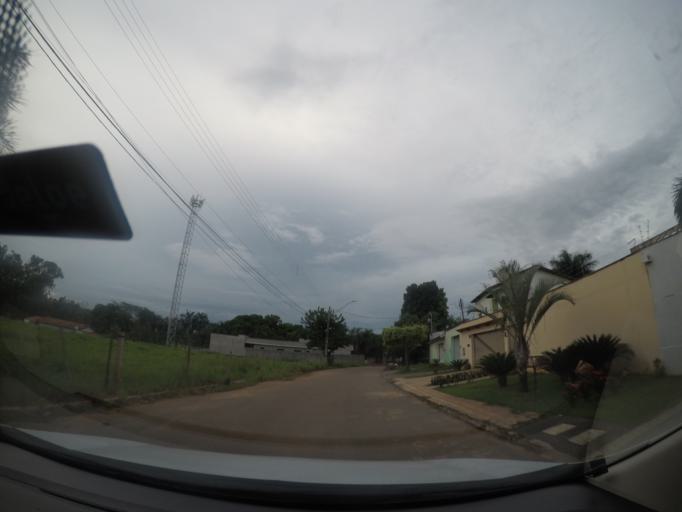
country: BR
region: Goias
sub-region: Goiania
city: Goiania
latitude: -16.6554
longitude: -49.2283
